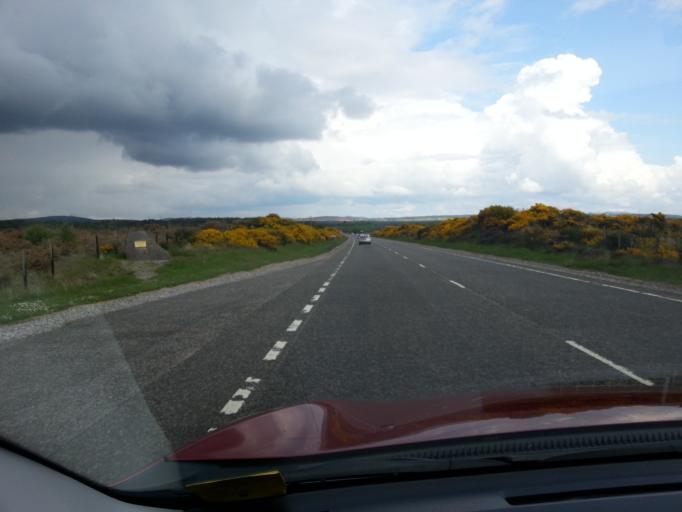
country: GB
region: Scotland
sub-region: Highland
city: Tain
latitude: 57.8568
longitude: -4.1117
